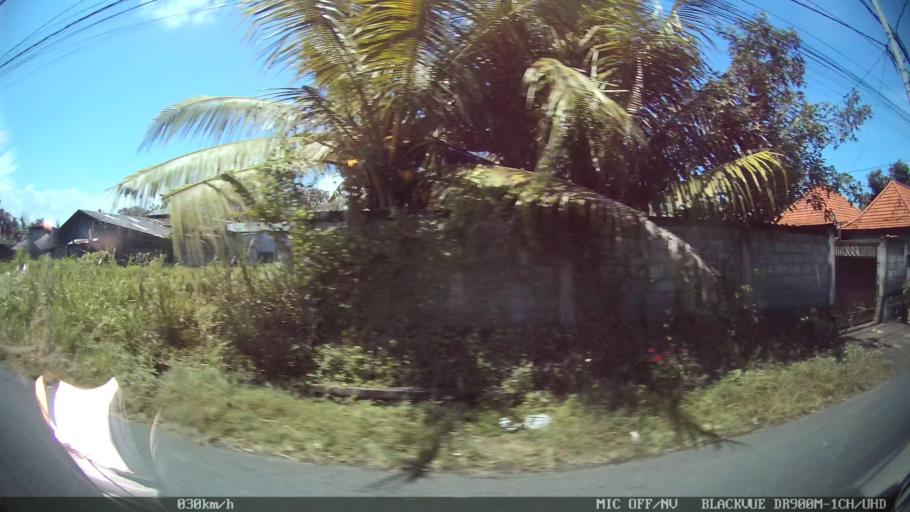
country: ID
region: Bali
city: Klungkung
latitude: -8.5605
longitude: 115.3383
